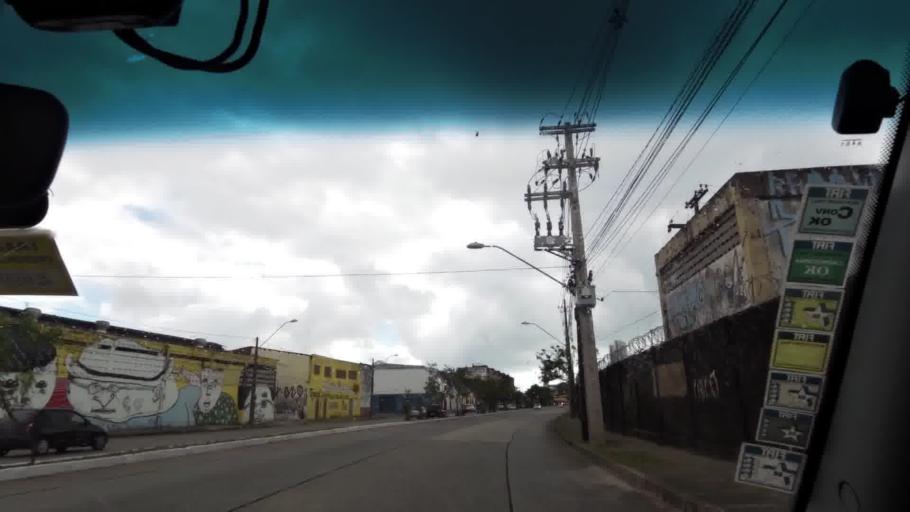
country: BR
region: Pernambuco
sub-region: Recife
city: Recife
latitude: -8.0742
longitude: -34.8861
